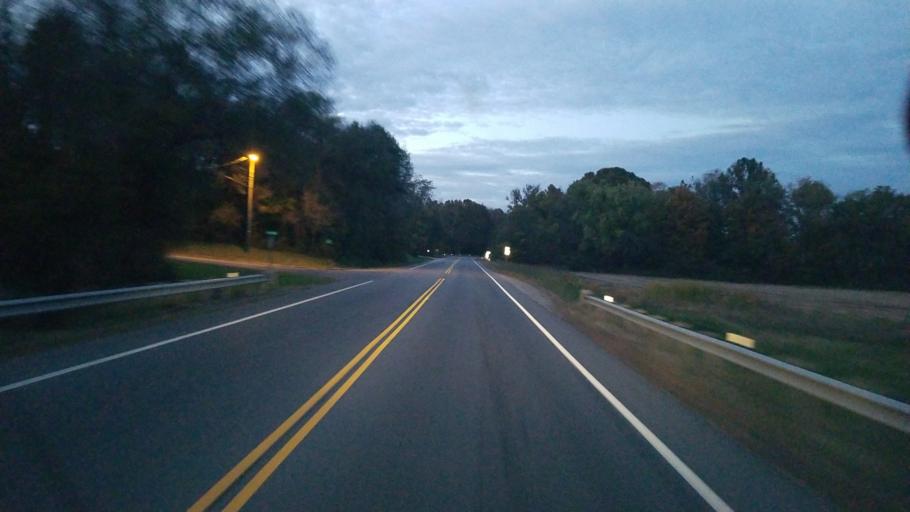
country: US
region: Ohio
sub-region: Scioto County
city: West Portsmouth
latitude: 38.7910
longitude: -83.0145
